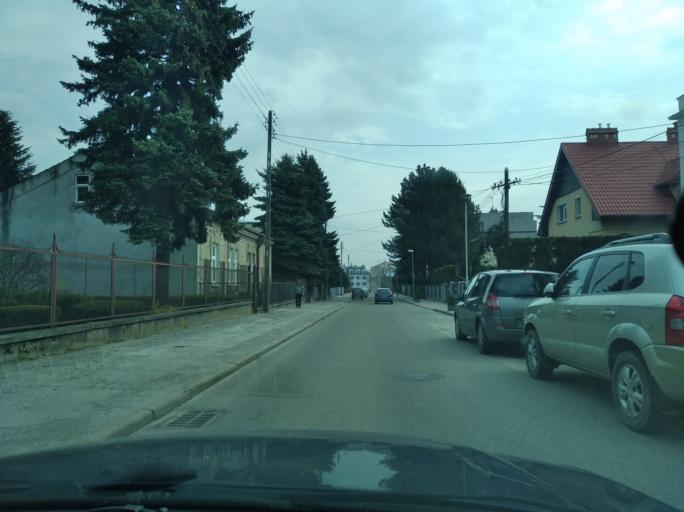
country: PL
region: Subcarpathian Voivodeship
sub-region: Powiat jaroslawski
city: Jaroslaw
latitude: 50.0142
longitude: 22.6857
